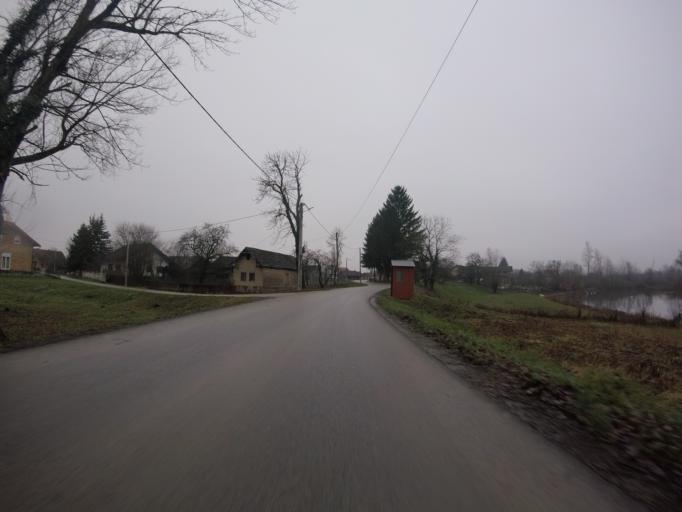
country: HR
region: Sisacko-Moslavacka
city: Lekenik
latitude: 45.6375
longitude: 16.2833
